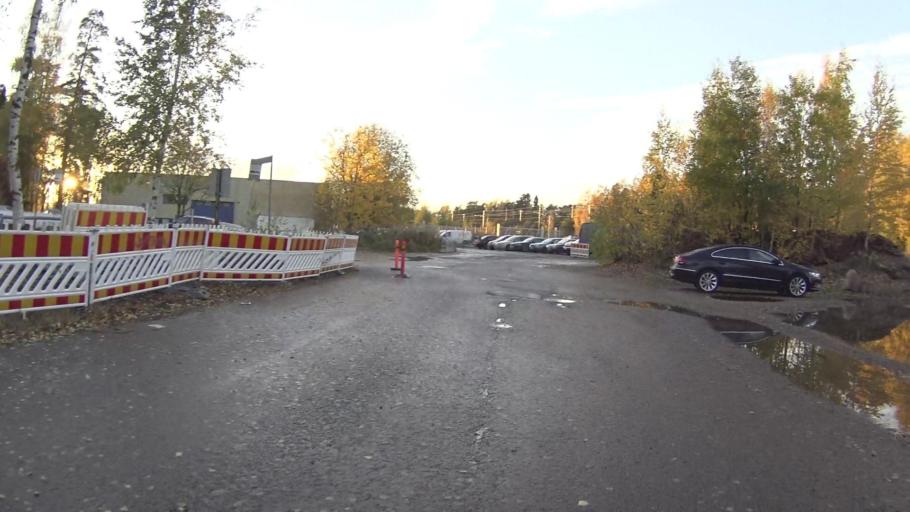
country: FI
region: Uusimaa
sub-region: Helsinki
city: Teekkarikylae
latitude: 60.2235
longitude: 24.8568
